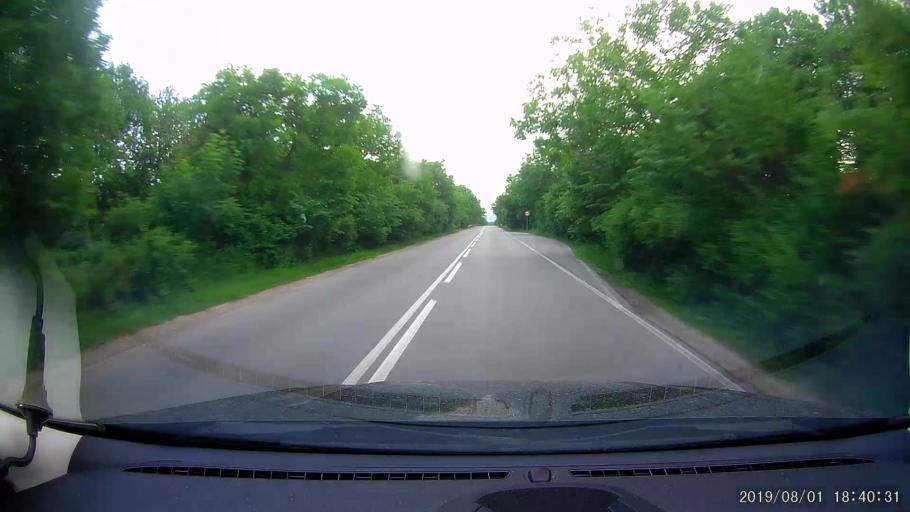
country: BG
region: Shumen
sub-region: Obshtina Khitrino
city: Gara Khitrino
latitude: 43.3656
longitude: 26.9195
